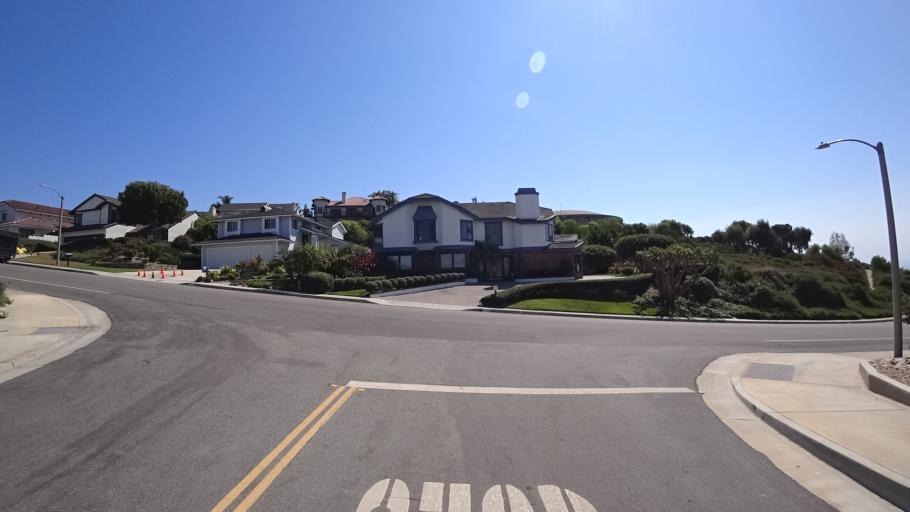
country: US
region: California
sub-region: Orange County
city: San Clemente
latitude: 33.4560
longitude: -117.6356
